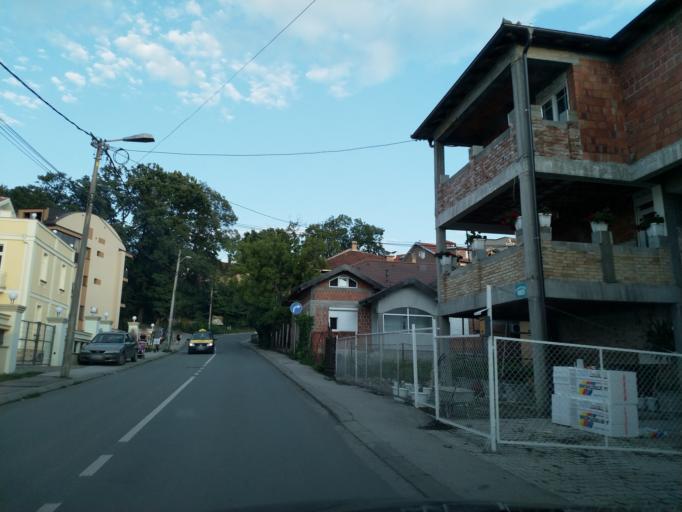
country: RS
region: Central Serbia
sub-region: Raski Okrug
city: Vrnjacka Banja
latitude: 43.6239
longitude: 20.8969
